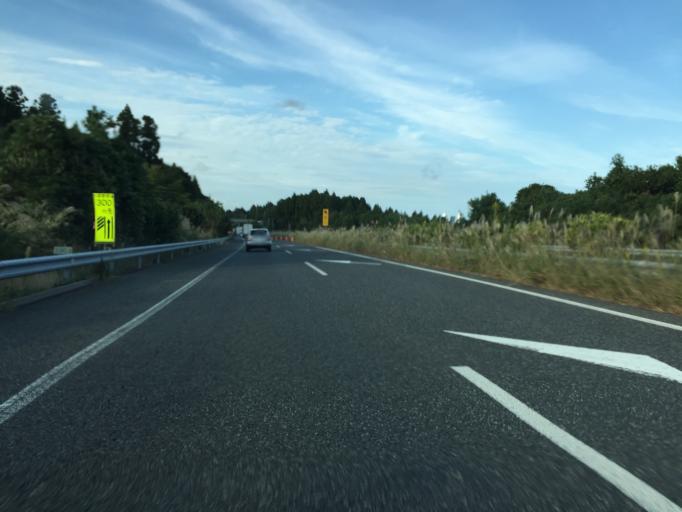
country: JP
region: Fukushima
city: Iwaki
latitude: 37.1925
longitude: 140.9860
